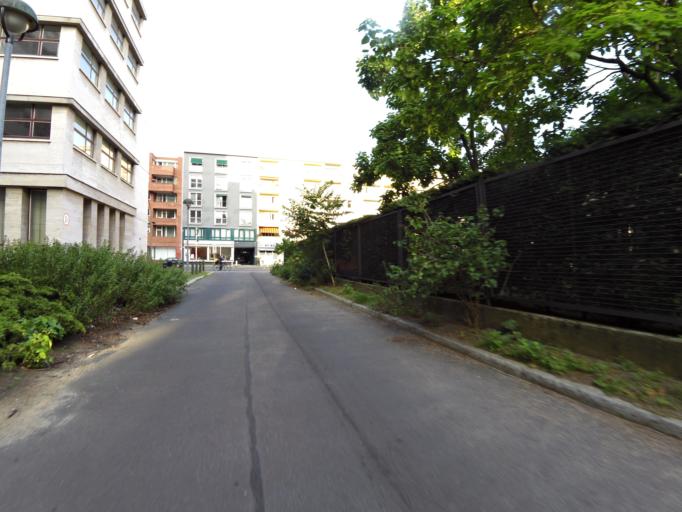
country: DE
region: Berlin
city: Berlin Schoeneberg
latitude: 52.4927
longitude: 13.3603
